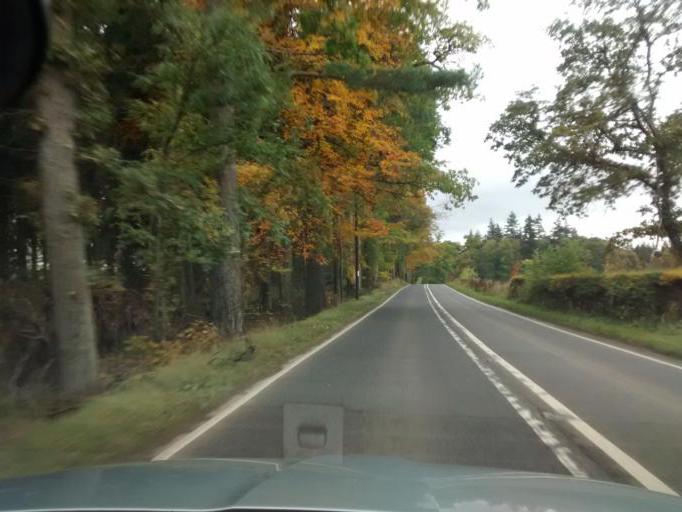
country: GB
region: Scotland
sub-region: Perth and Kinross
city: Blairgowrie
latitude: 56.5384
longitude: -3.3609
